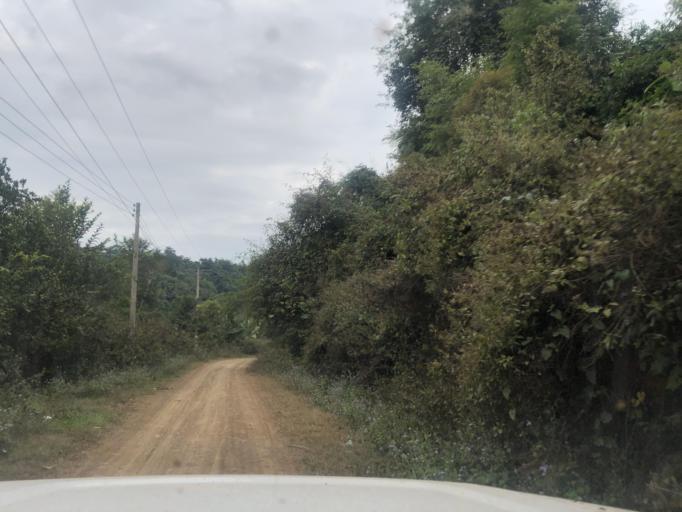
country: LA
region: Phongsali
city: Khoa
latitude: 21.3029
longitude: 102.5843
